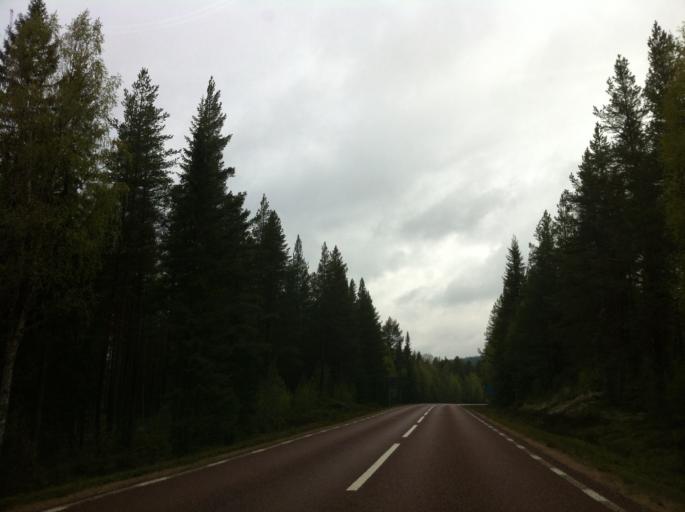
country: SE
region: Jaemtland
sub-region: Harjedalens Kommun
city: Sveg
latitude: 61.8664
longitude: 14.6376
